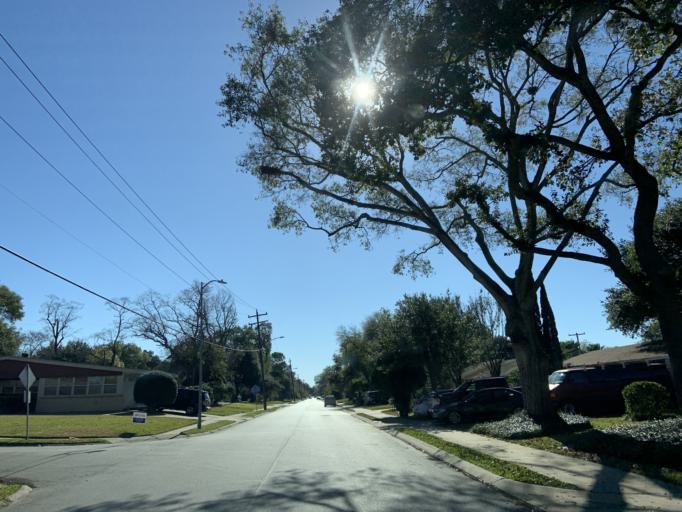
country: US
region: Texas
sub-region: Harris County
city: Bellaire
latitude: 29.6959
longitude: -95.5045
